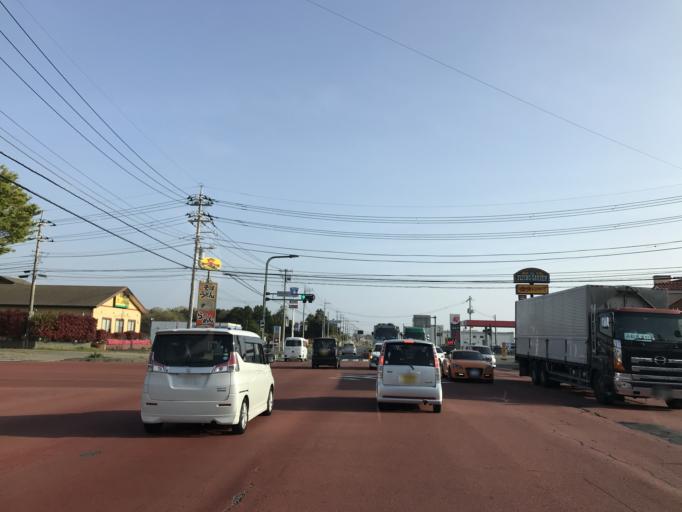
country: JP
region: Ibaraki
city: Hitachi-Naka
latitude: 36.4012
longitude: 140.5805
